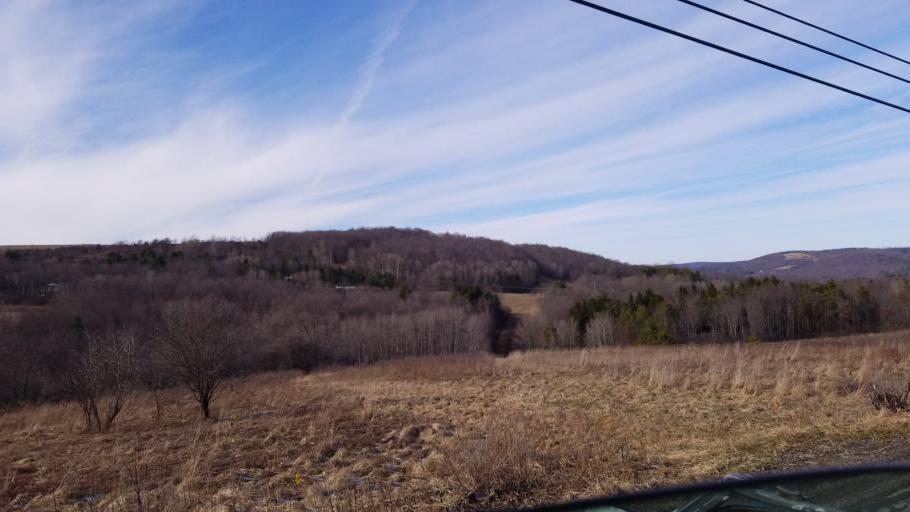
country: US
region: New York
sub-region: Allegany County
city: Wellsville
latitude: 42.1023
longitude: -77.9702
